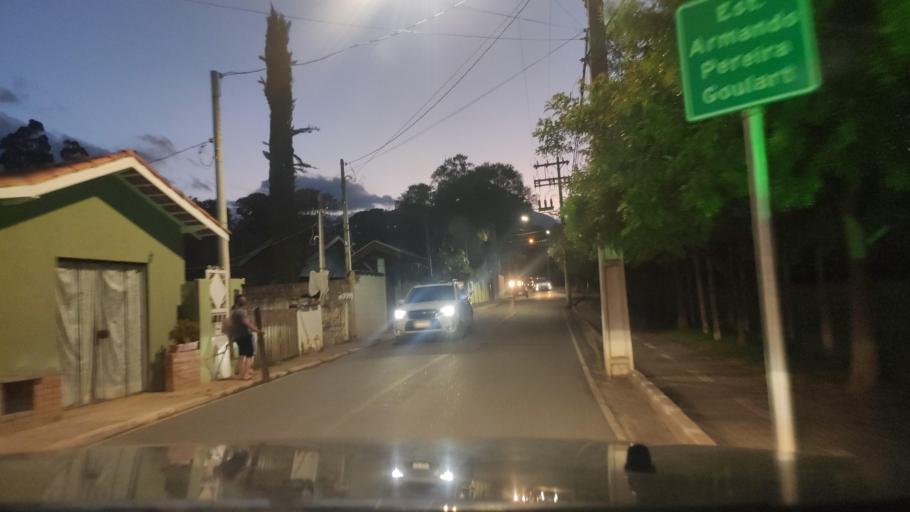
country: BR
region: Minas Gerais
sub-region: Paraisopolis
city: Paraisopolis
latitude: -22.6936
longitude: -45.7429
